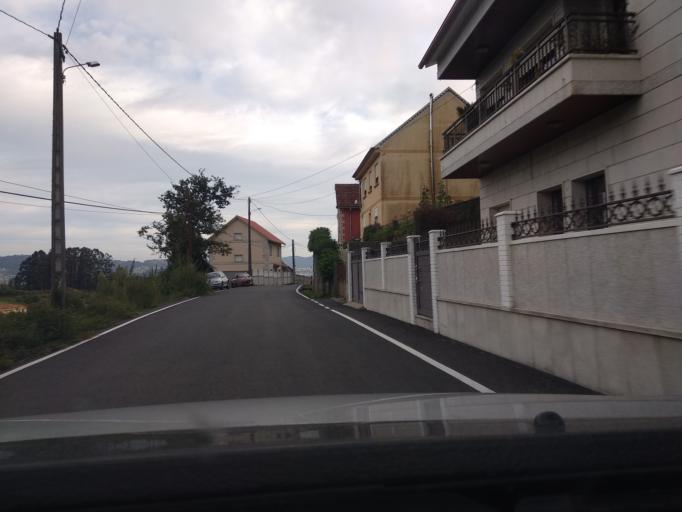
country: ES
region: Galicia
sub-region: Provincia de Pontevedra
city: Moana
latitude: 42.2962
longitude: -8.7390
